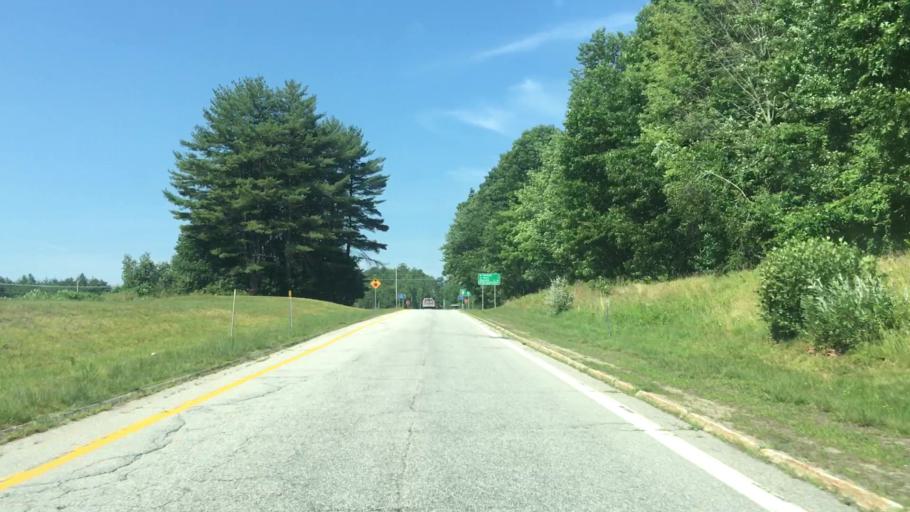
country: US
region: New Hampshire
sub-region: Merrimack County
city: Henniker
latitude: 43.1893
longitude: -71.8252
